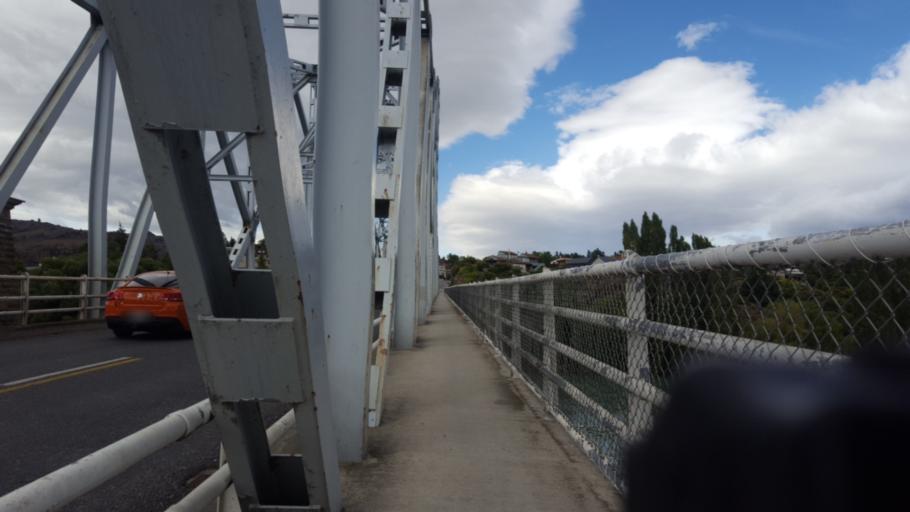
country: NZ
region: Otago
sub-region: Queenstown-Lakes District
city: Wanaka
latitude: -45.2579
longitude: 169.3911
